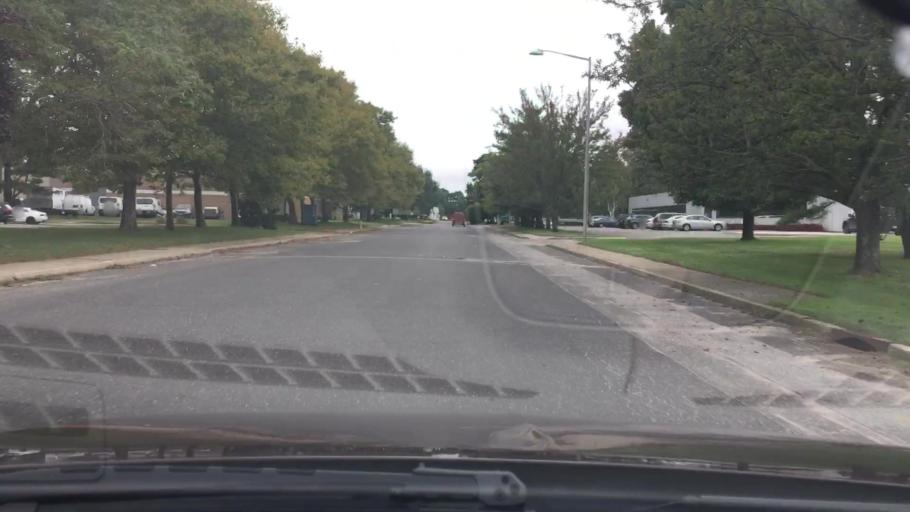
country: US
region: New York
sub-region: Suffolk County
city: Islandia
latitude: 40.7934
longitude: -73.1419
